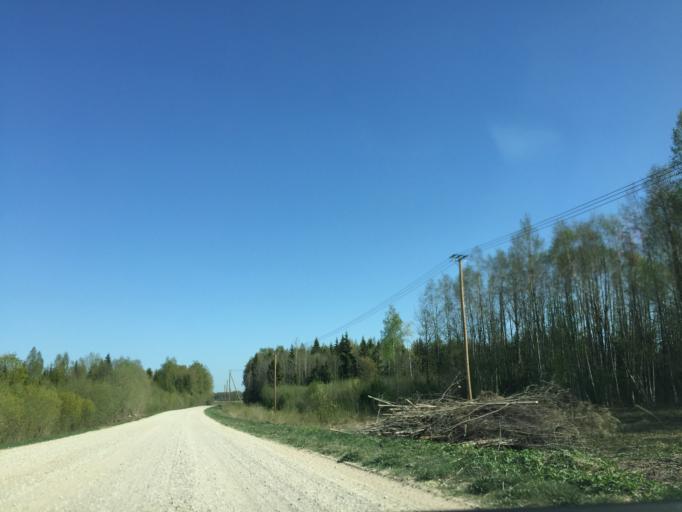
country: LV
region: Malpils
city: Malpils
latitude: 56.8491
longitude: 25.0733
